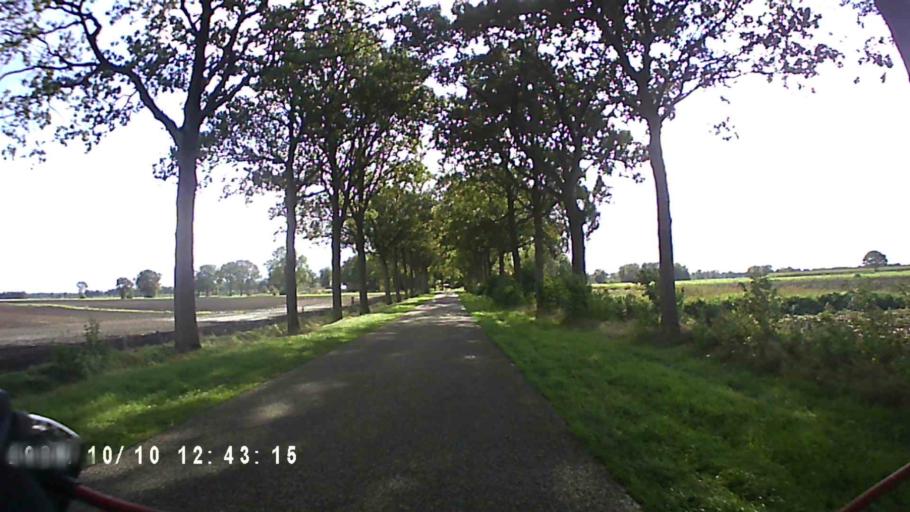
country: NL
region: Friesland
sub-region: Gemeente Weststellingwerf
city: Noordwolde
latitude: 52.9324
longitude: 6.2212
